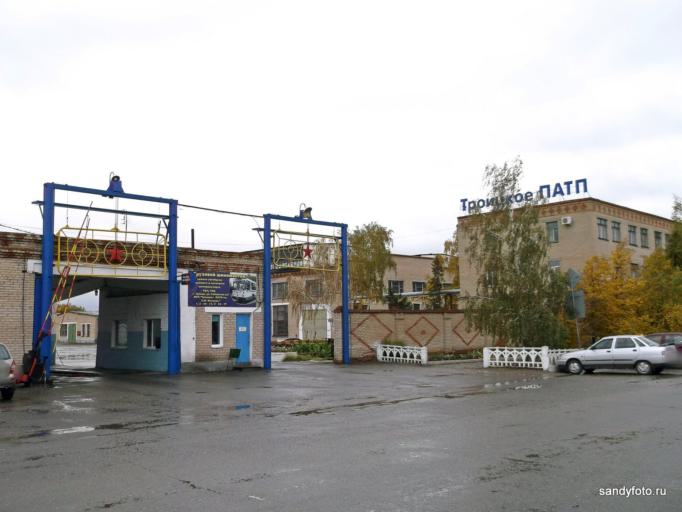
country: RU
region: Chelyabinsk
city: Troitsk
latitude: 54.0877
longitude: 61.5754
